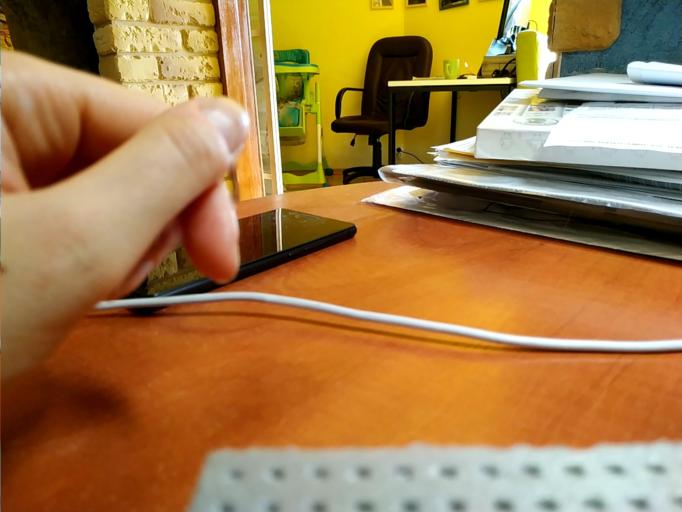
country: RU
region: Tverskaya
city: Likhoslavl'
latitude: 57.3639
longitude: 35.4545
